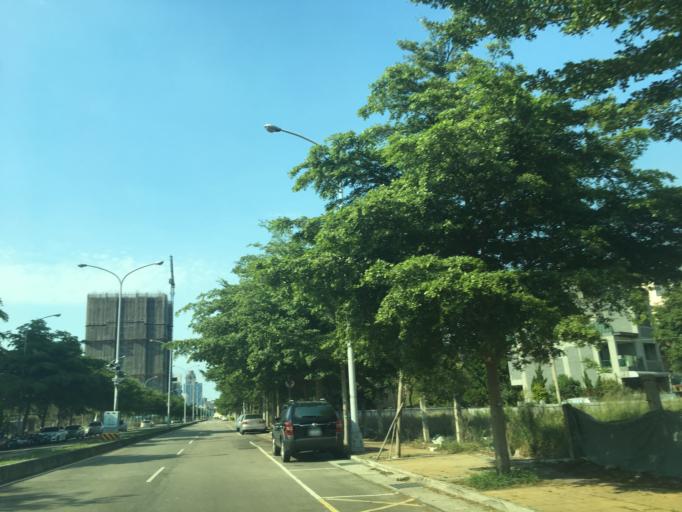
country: TW
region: Taiwan
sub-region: Taichung City
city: Taichung
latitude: 24.1541
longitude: 120.6275
